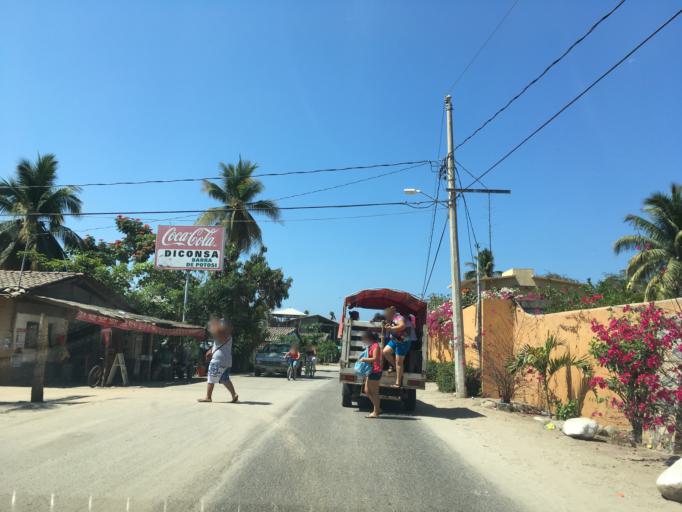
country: MX
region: Guerrero
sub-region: Zihuatanejo de Azueta
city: Los Achotes
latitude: 17.5385
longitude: -101.4412
